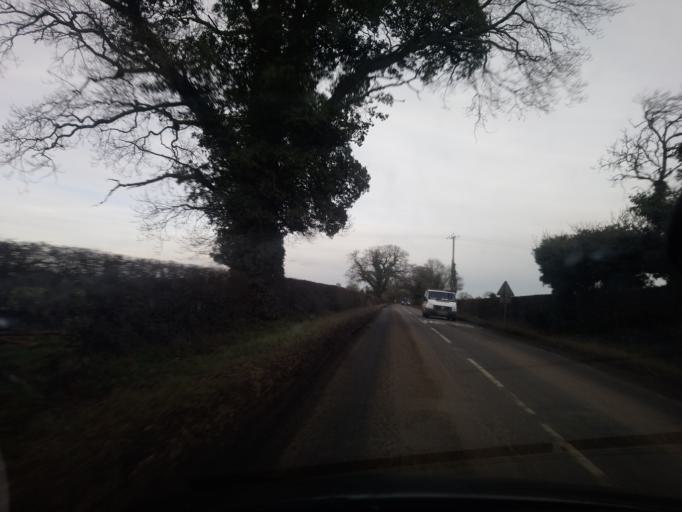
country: GB
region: England
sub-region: Shropshire
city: Prees
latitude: 52.9084
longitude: -2.6903
